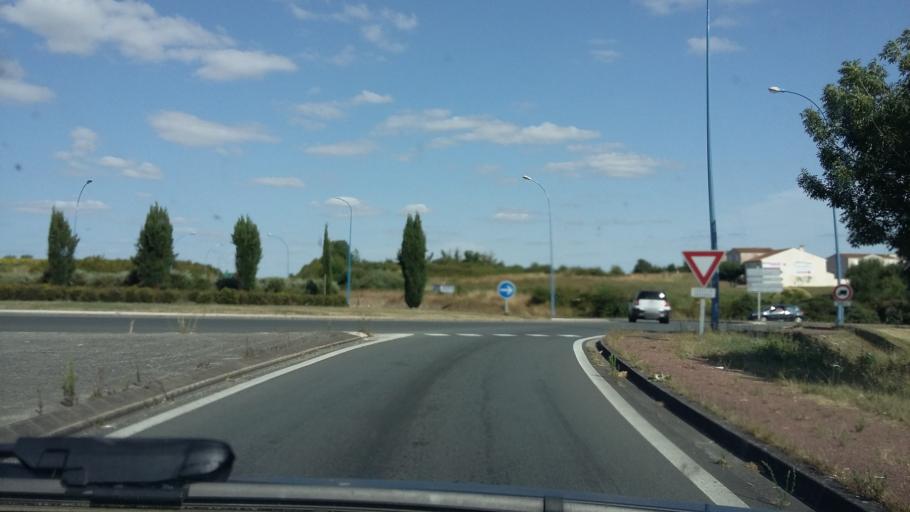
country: FR
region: Poitou-Charentes
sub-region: Departement de la Charente-Maritime
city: Saint-Jean-d'Angely
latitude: 45.9562
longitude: -0.5292
